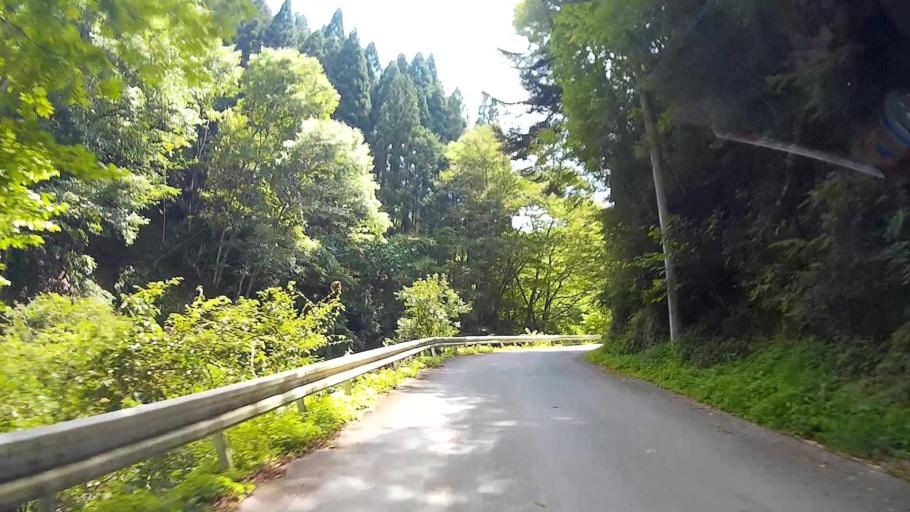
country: JP
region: Saitama
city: Chichibu
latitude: 35.8978
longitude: 139.0991
